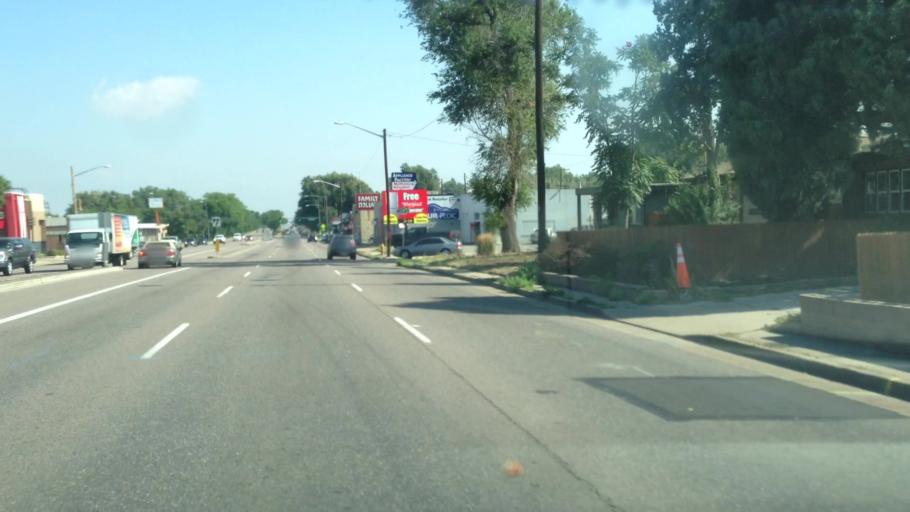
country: US
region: Colorado
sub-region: Denver County
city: Denver
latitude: 39.7559
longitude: -104.9405
